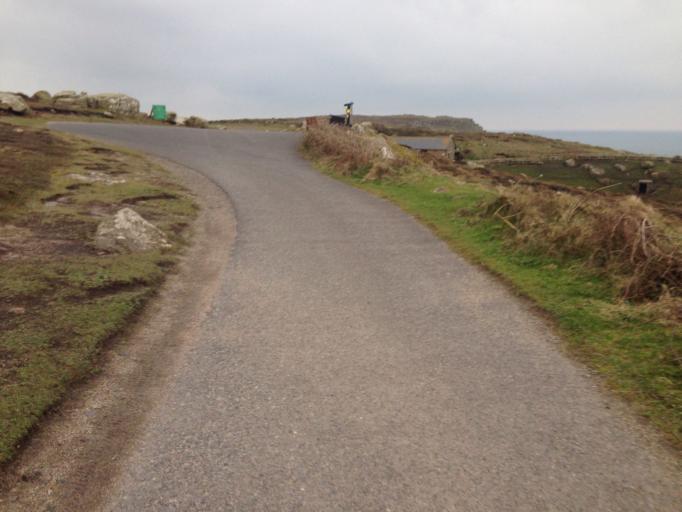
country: GB
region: England
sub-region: Cornwall
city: Sennen
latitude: 50.0636
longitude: -5.7116
